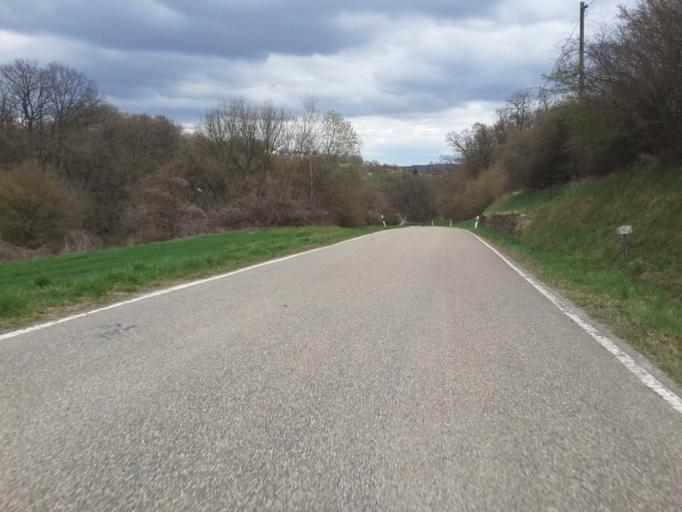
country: DE
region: Baden-Wuerttemberg
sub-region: Regierungsbezirk Stuttgart
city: Roigheim
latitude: 49.3690
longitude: 9.3283
